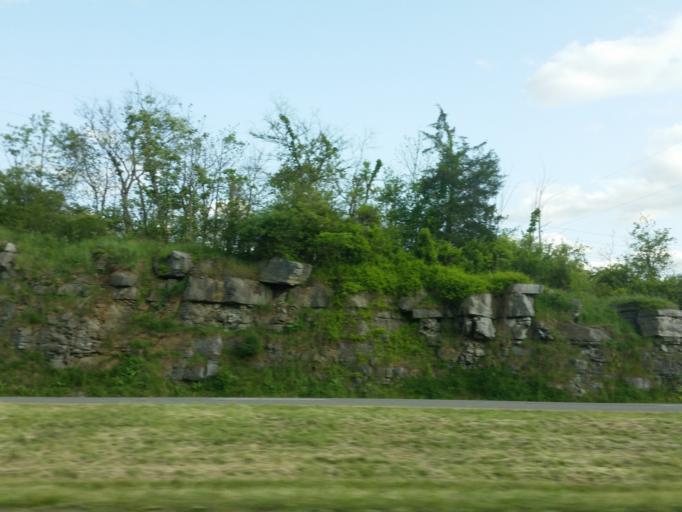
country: US
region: Virginia
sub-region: Tazewell County
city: Tazewell
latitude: 37.1214
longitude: -81.5721
